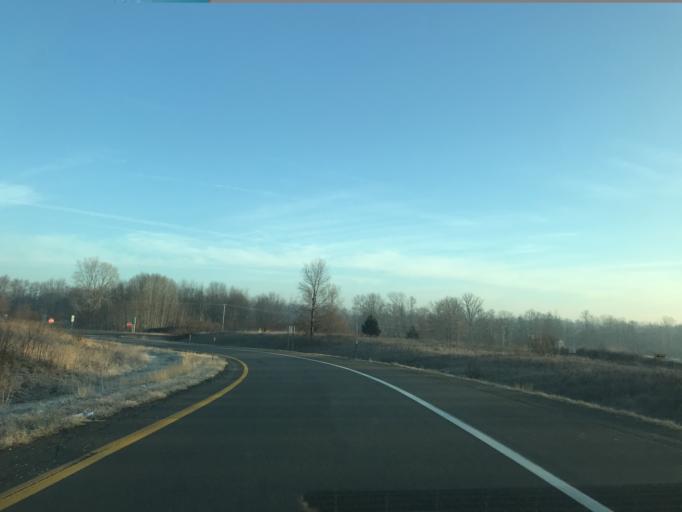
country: US
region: Michigan
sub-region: Ingham County
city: Leslie
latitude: 42.3773
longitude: -84.4271
